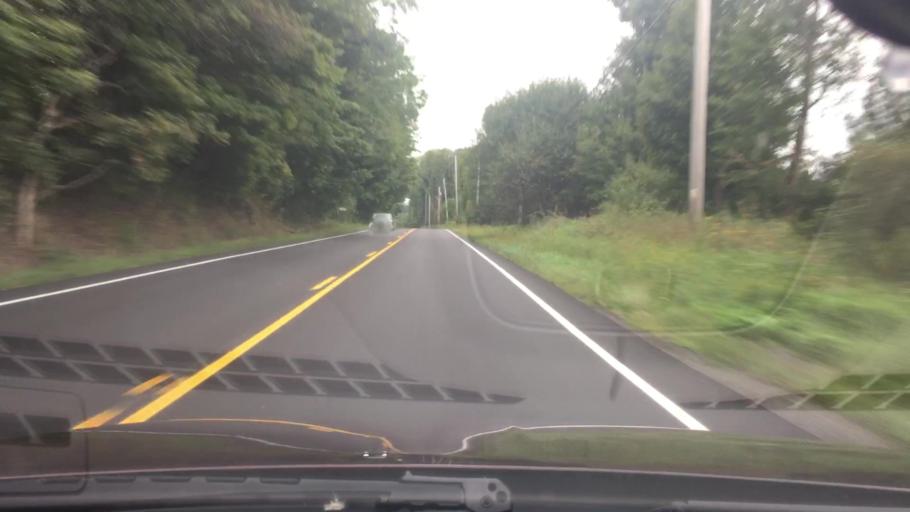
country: US
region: New York
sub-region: Dutchess County
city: Millbrook
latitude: 41.8348
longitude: -73.6140
